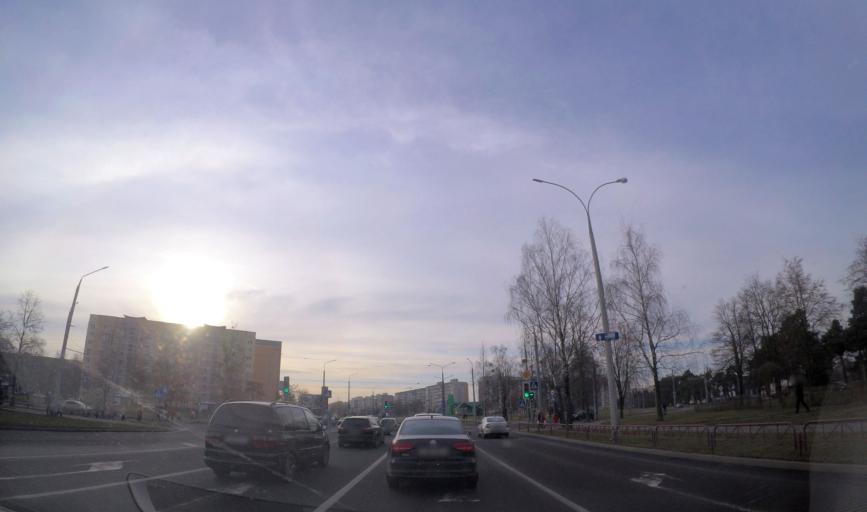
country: BY
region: Grodnenskaya
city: Hrodna
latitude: 53.6663
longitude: 23.7867
